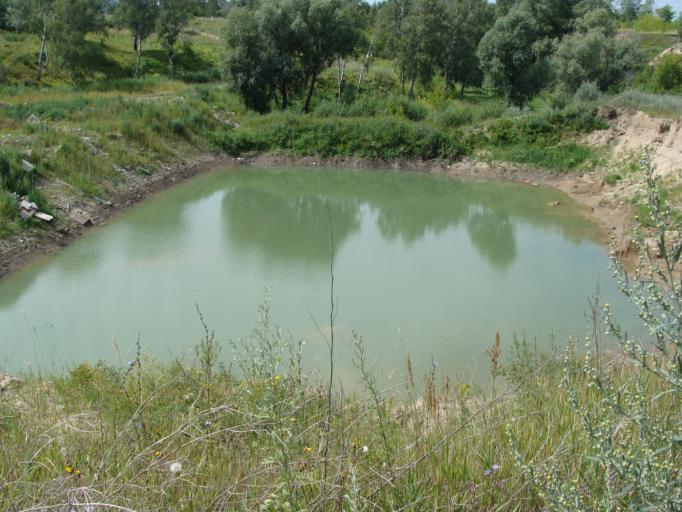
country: RU
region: Altai Krai
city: Novosilikatnyy
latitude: 53.3349
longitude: 83.6444
